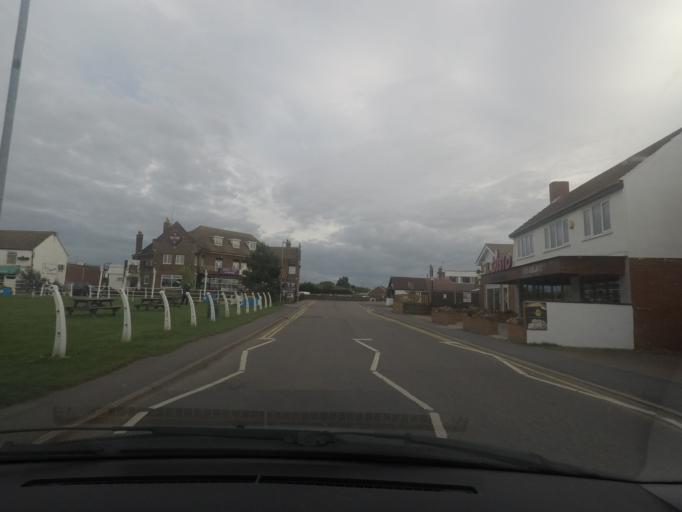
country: GB
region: England
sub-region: Lincolnshire
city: Chapel Saint Leonards
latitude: 53.2237
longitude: 0.3366
